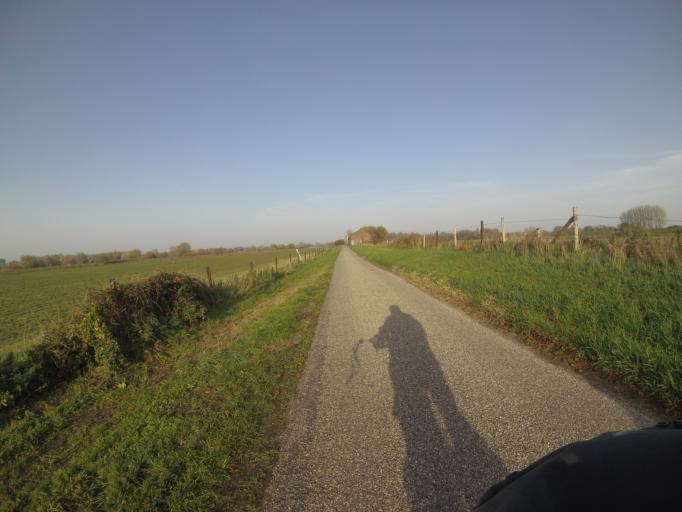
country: NL
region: Gelderland
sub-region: Gemeente Maasdriel
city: Heerewaarden
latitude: 51.8285
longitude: 5.3934
